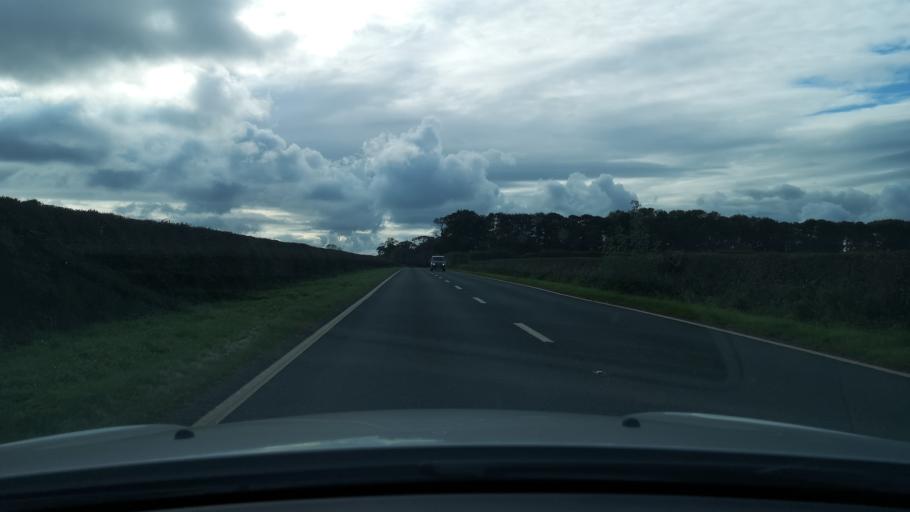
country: GB
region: England
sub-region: East Riding of Yorkshire
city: Walkington
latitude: 53.8096
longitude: -0.5372
